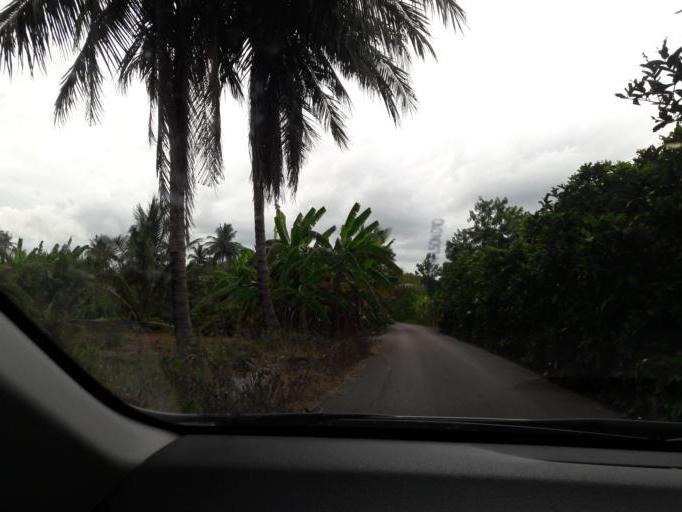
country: TH
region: Ratchaburi
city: Damnoen Saduak
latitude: 13.5443
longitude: 99.9992
